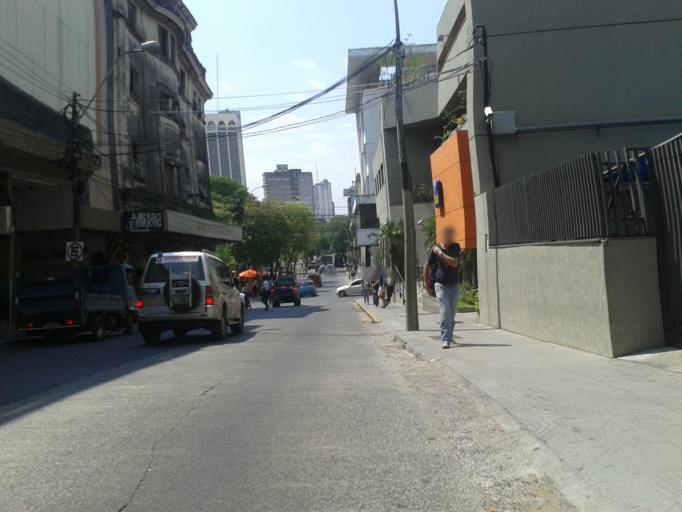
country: PY
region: Asuncion
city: Asuncion
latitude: -25.2829
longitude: -57.6366
